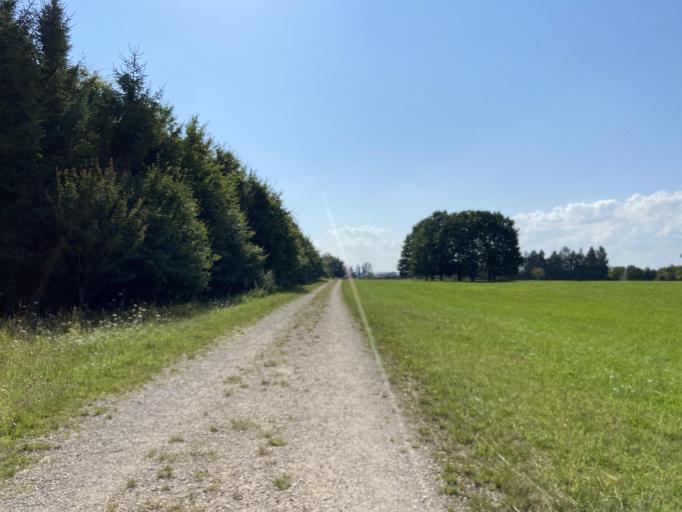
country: DE
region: Baden-Wuerttemberg
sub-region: Tuebingen Region
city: Sigmaringen
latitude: 48.0868
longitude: 9.2462
